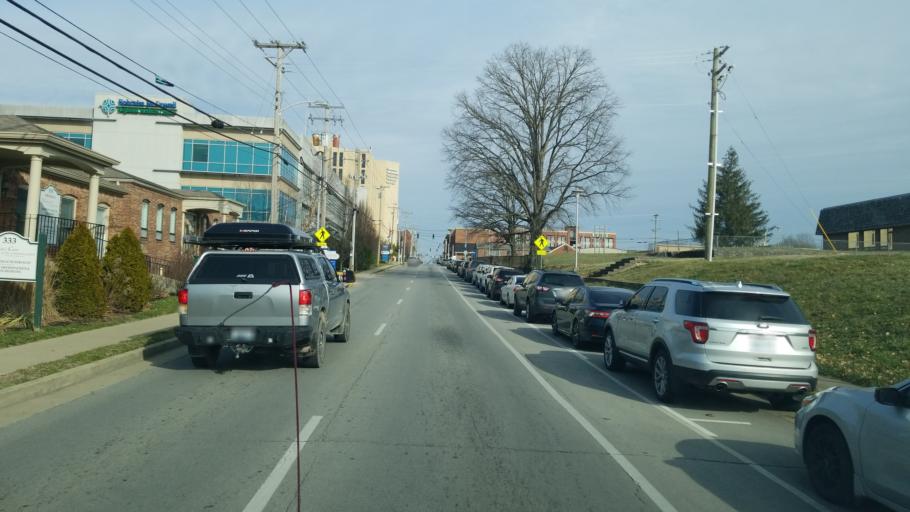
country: US
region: Kentucky
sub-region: Boyle County
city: Danville
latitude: 37.6423
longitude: -84.7729
